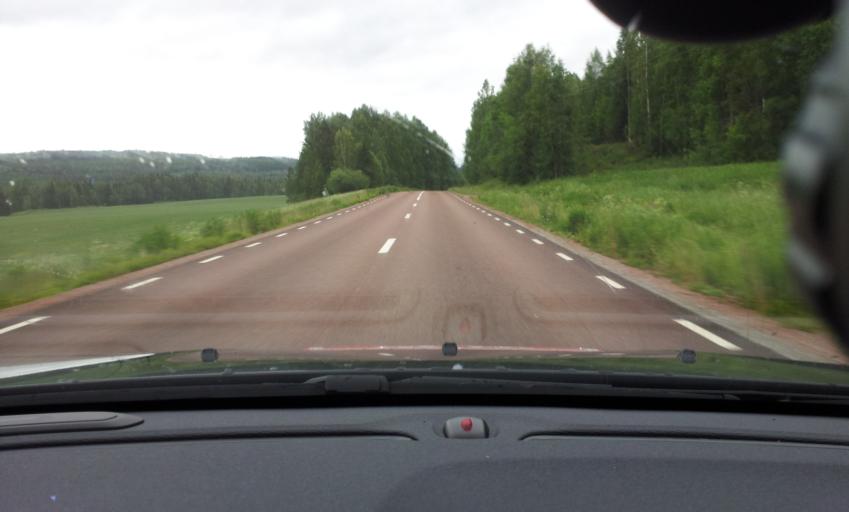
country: SE
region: Jaemtland
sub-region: Ragunda Kommun
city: Hammarstrand
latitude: 63.0587
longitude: 16.4703
